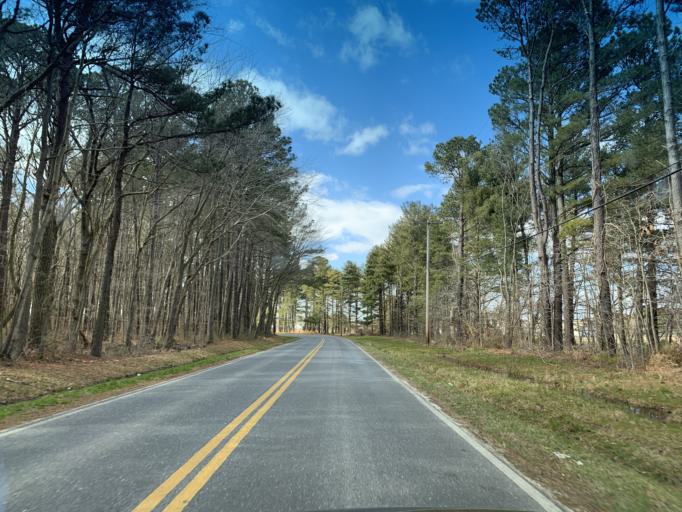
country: US
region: Maryland
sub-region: Queen Anne's County
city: Chester
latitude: 38.9485
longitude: -76.2725
